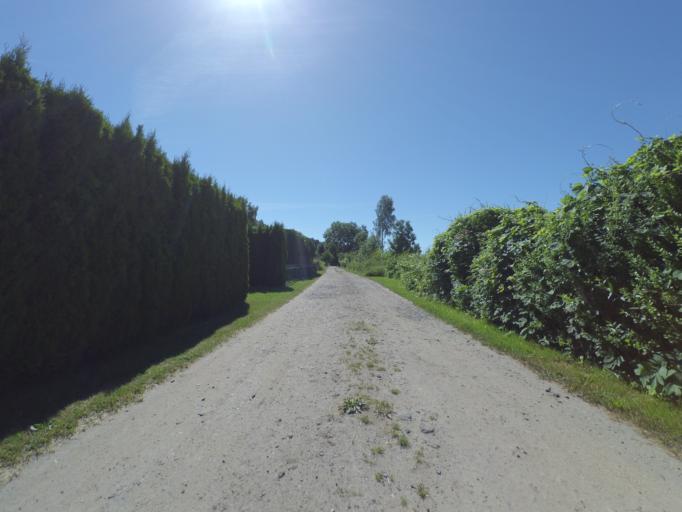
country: DE
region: Mecklenburg-Vorpommern
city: Plau am See
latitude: 53.5178
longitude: 12.3269
